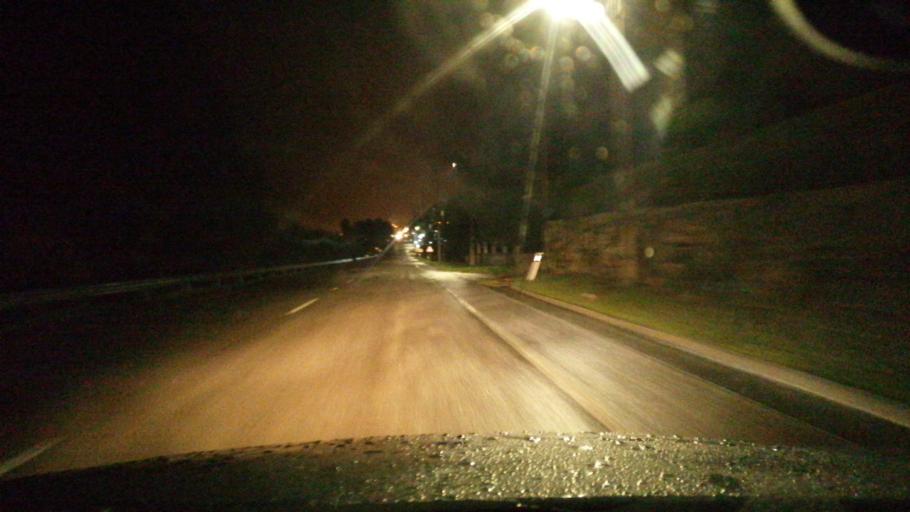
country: PT
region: Viseu
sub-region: Sernancelhe
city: Sernancelhe
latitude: 40.9041
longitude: -7.4682
